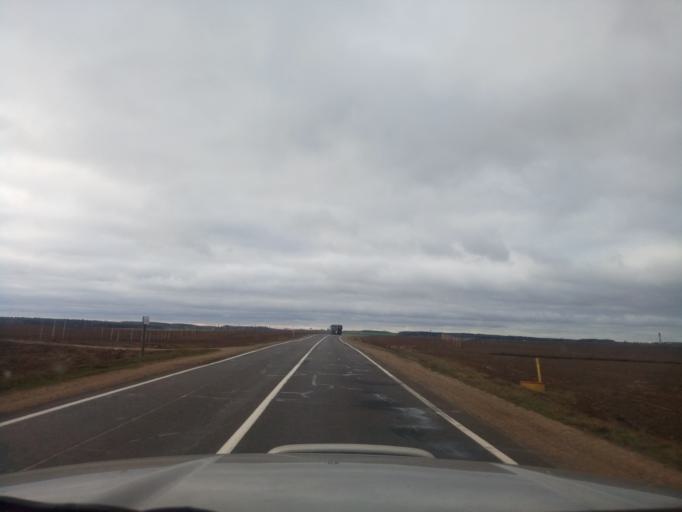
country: BY
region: Minsk
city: Kapyl'
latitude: 53.2018
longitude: 27.2172
